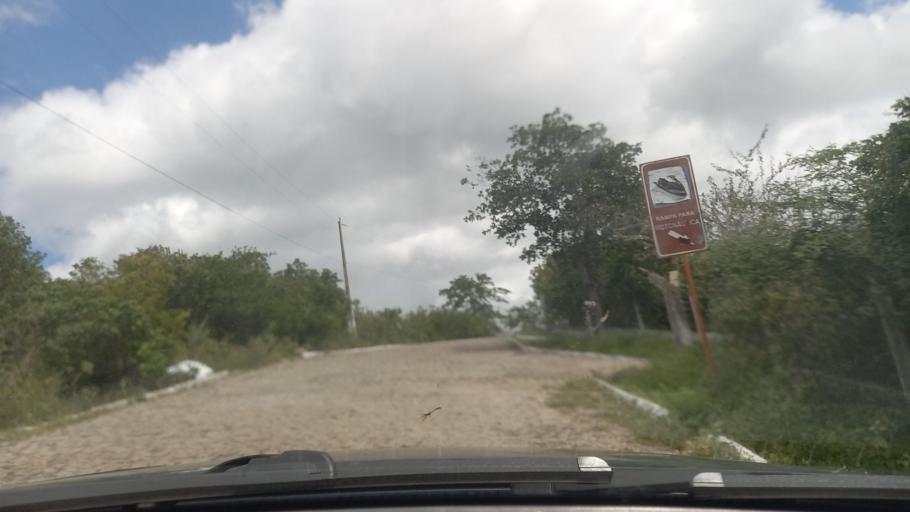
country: BR
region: Sergipe
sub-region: Caninde De Sao Francisco
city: Caninde de Sao Francisco
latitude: -9.6186
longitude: -37.8100
